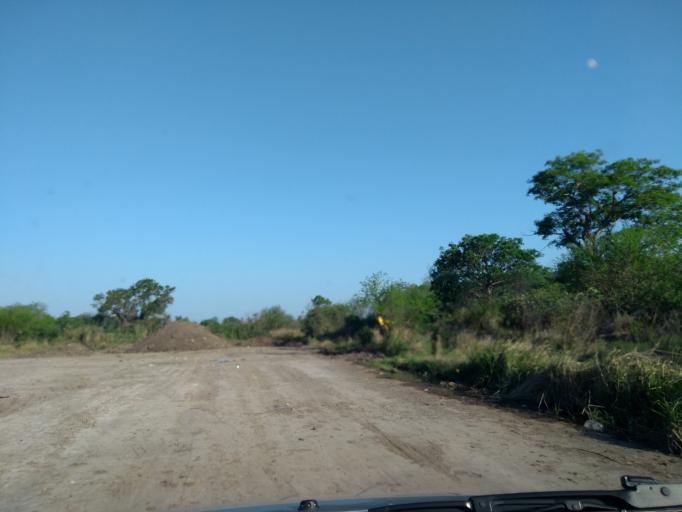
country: AR
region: Chaco
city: Fontana
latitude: -27.4163
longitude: -59.0584
